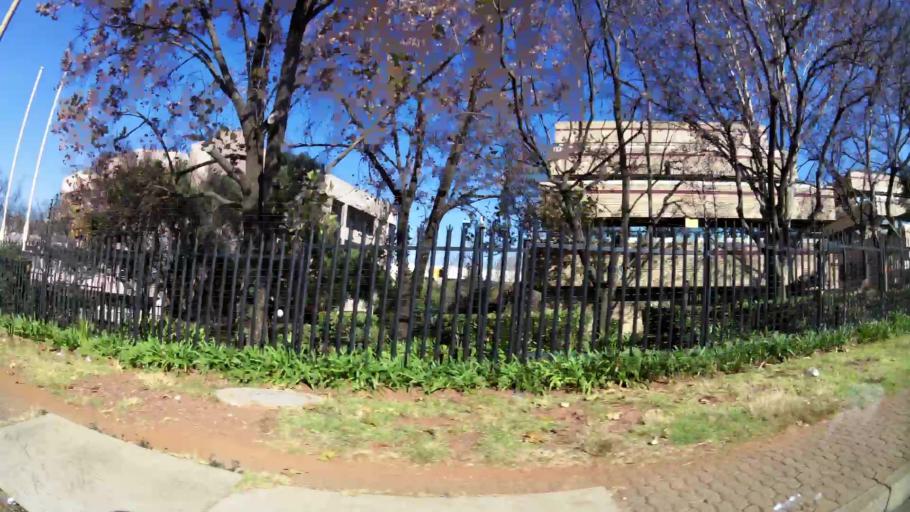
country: ZA
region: Gauteng
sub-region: City of Johannesburg Metropolitan Municipality
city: Johannesburg
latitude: -26.1829
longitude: 28.0401
